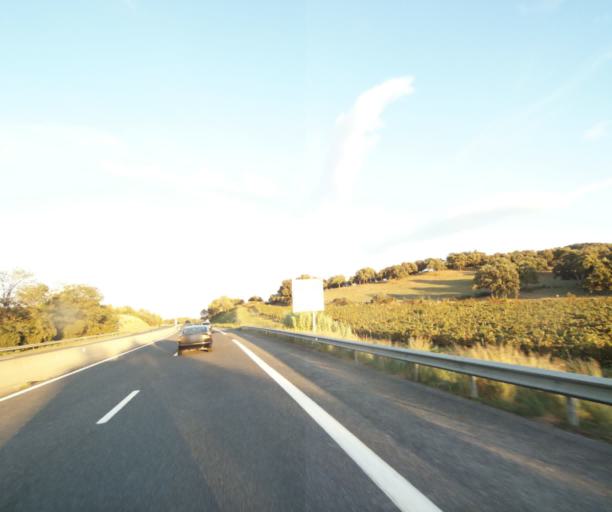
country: FR
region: Languedoc-Roussillon
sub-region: Departement des Pyrenees-Orientales
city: Argelers
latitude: 42.5352
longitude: 3.0368
